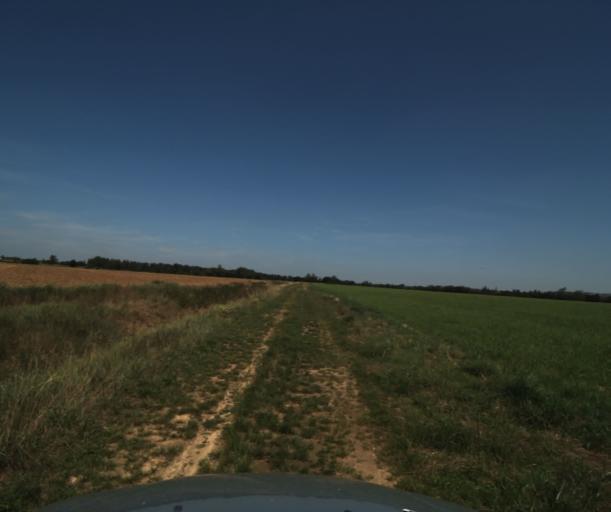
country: FR
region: Midi-Pyrenees
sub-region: Departement de la Haute-Garonne
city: Labastidette
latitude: 43.4428
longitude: 1.2721
